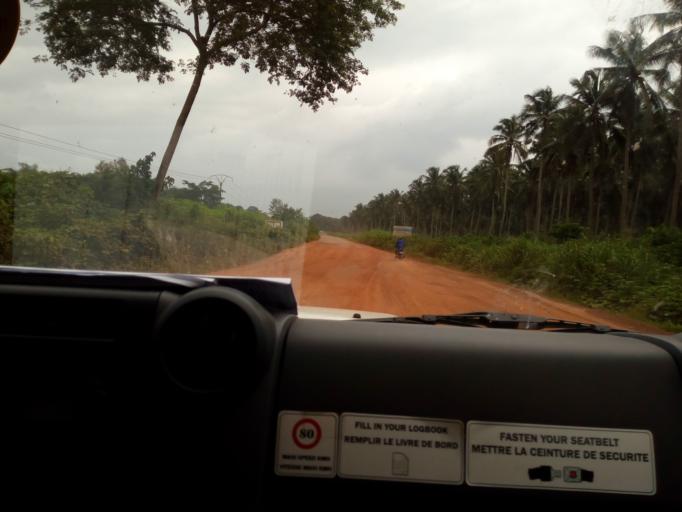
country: CI
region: Bas-Sassandra
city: Tabou
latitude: 4.5308
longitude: -7.2263
